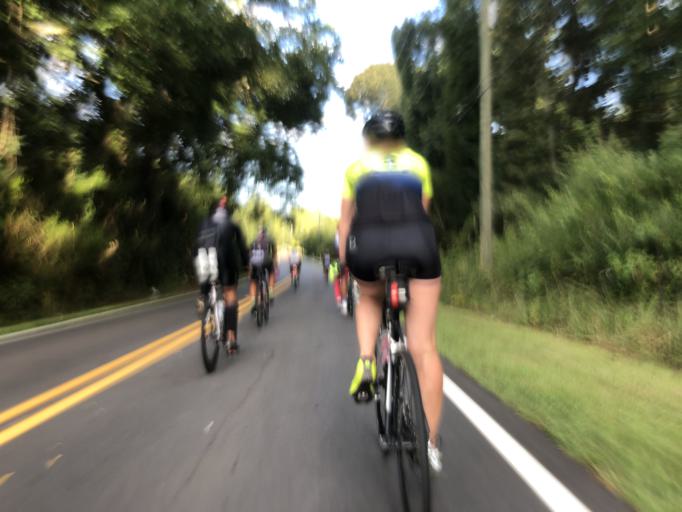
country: US
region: Georgia
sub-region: Fulton County
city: Palmetto
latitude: 33.5729
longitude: -84.6513
